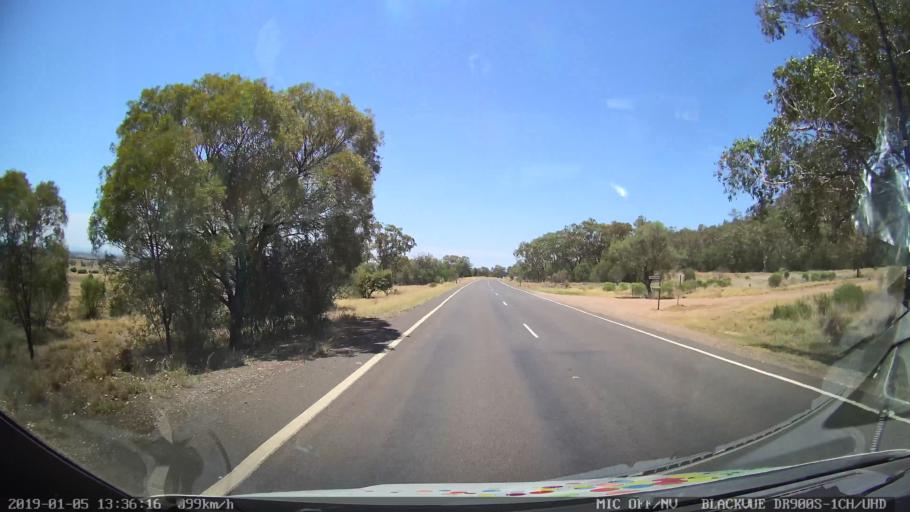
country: AU
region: New South Wales
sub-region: Gunnedah
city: Gunnedah
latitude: -30.9861
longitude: 150.1620
